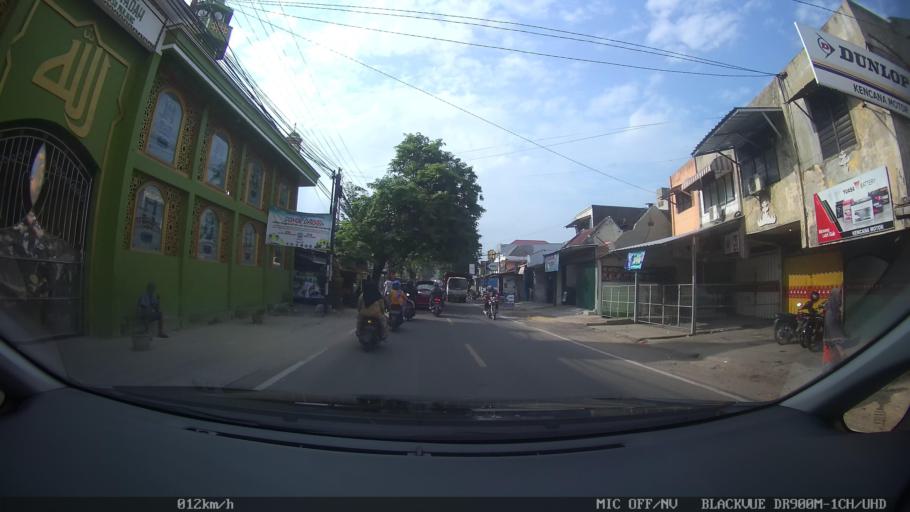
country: ID
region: Lampung
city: Panjang
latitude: -5.4754
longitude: 105.3222
